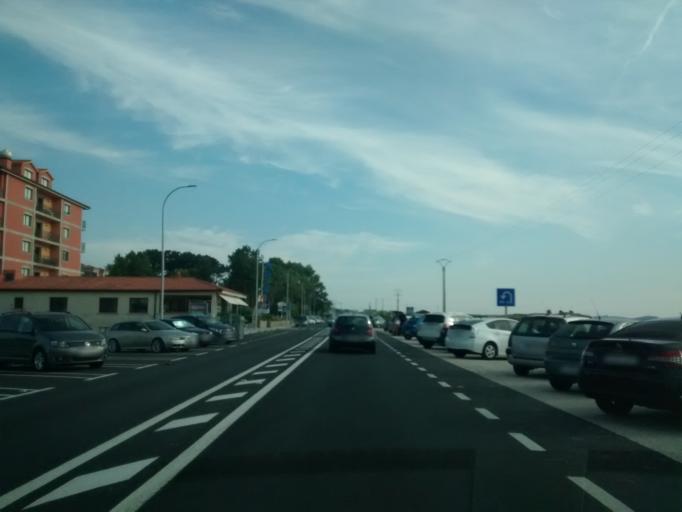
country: ES
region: Galicia
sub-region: Provincia de Pontevedra
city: O Grove
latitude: 42.4330
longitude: -8.8712
